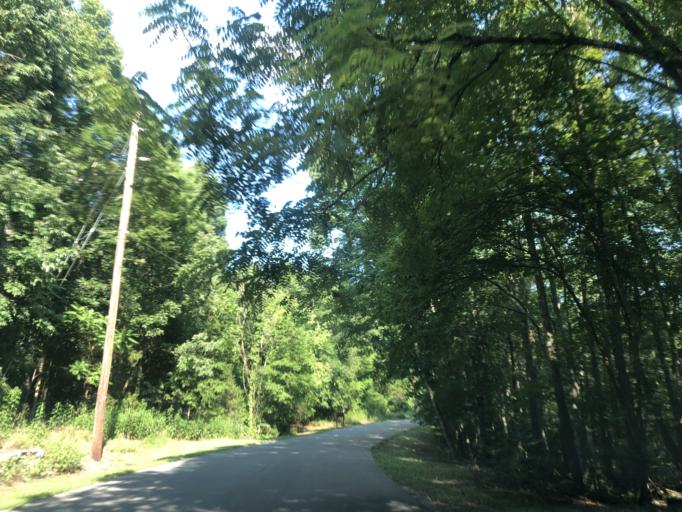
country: US
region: Tennessee
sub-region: Wilson County
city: Green Hill
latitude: 36.1374
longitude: -86.5971
